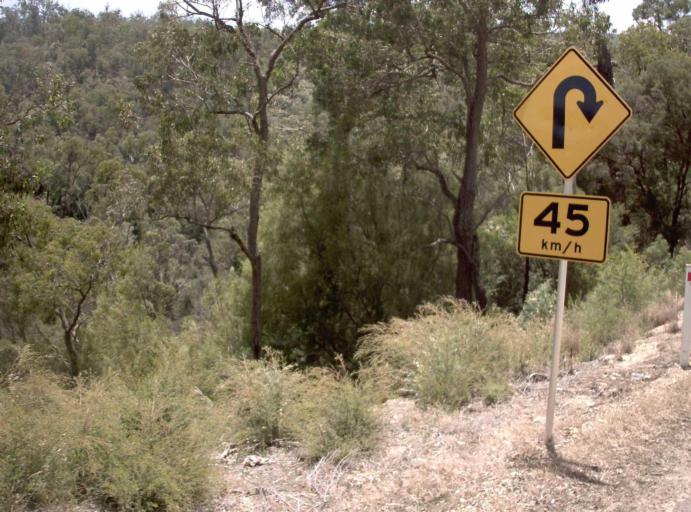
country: AU
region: Victoria
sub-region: East Gippsland
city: Lakes Entrance
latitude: -37.5562
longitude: 147.8853
